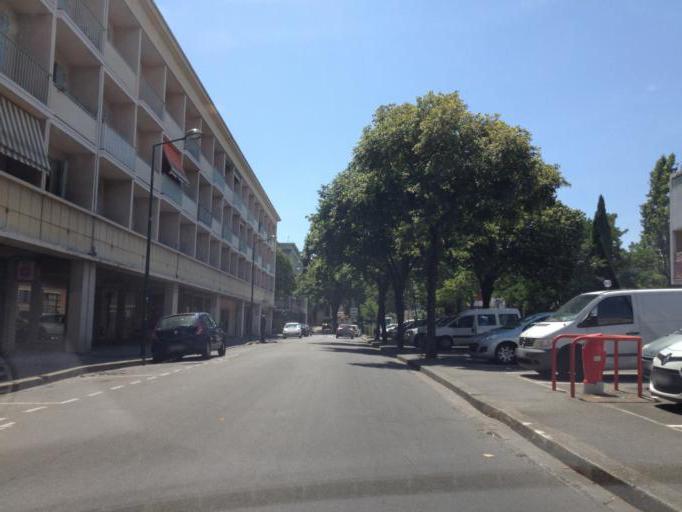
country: FR
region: Rhone-Alpes
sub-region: Departement de la Drome
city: Valence
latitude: 44.9345
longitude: 4.8945
